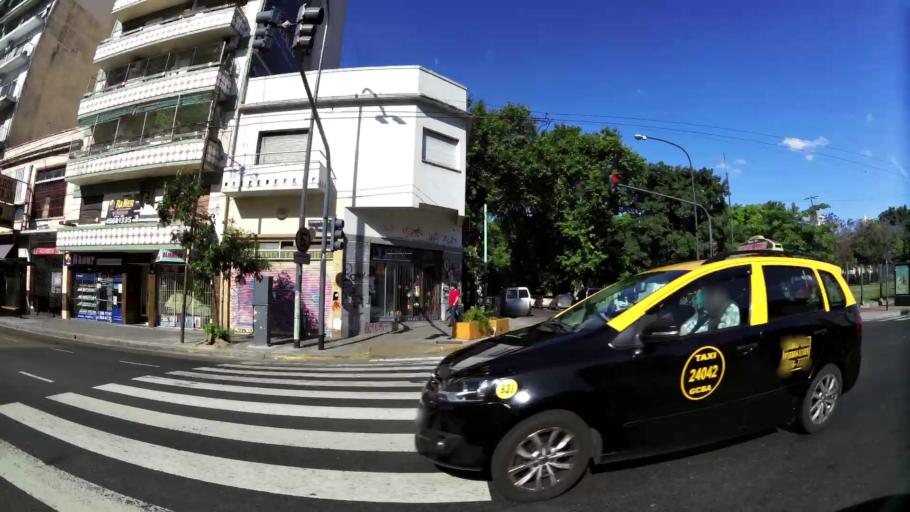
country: AR
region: Buenos Aires F.D.
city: Villa Santa Rita
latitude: -34.6212
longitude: -58.4738
